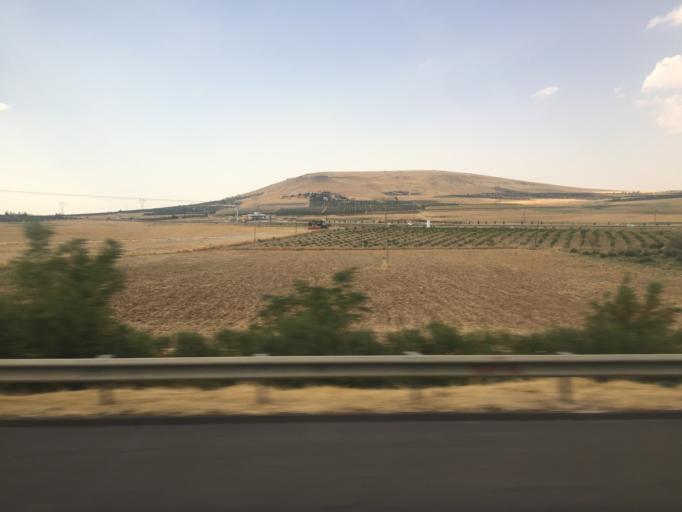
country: TR
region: Sanliurfa
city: Akziyaret
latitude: 37.2639
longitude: 38.7650
